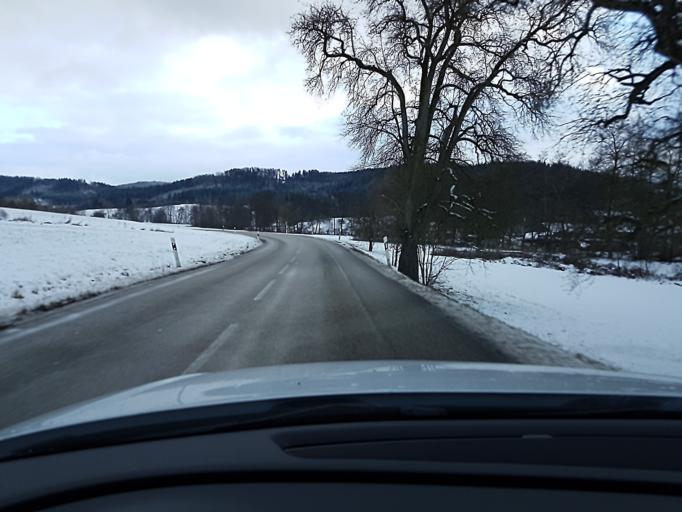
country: DE
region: Baden-Wuerttemberg
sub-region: Regierungsbezirk Stuttgart
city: Kaisersbach
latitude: 48.9666
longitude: 9.6433
